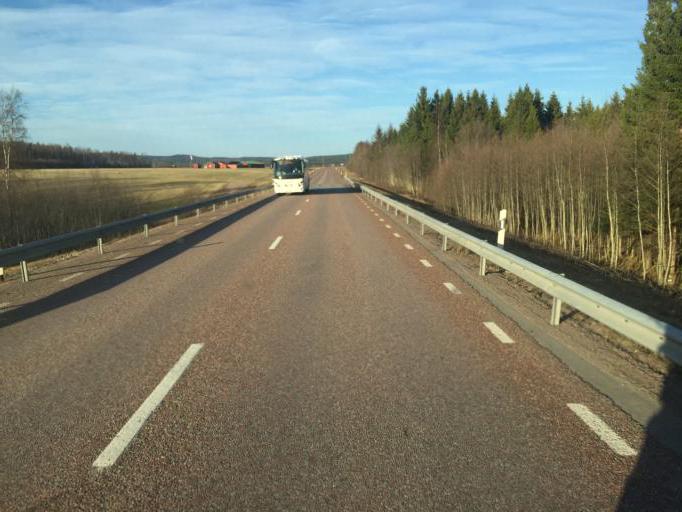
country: SE
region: Dalarna
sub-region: Gagnefs Kommun
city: Gagnef
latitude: 60.5478
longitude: 15.0744
